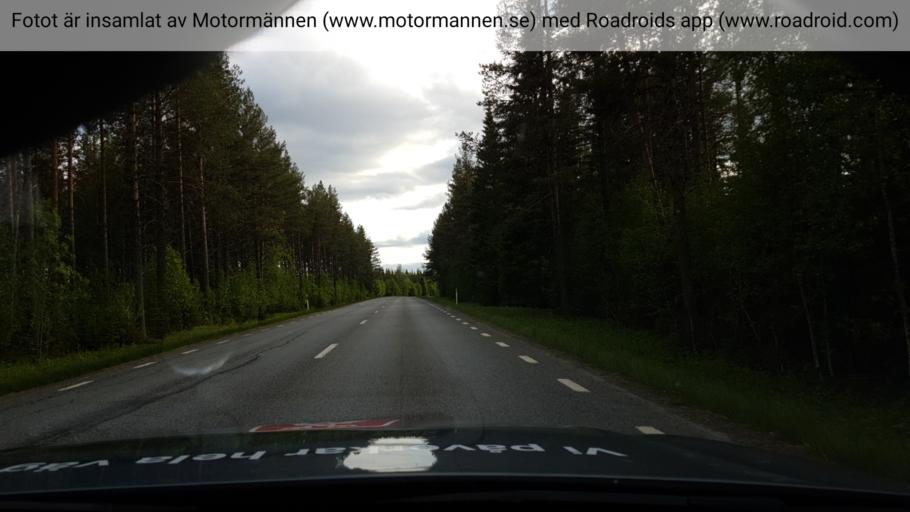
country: SE
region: Jaemtland
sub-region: Stroemsunds Kommun
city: Stroemsund
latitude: 63.5302
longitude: 15.3297
